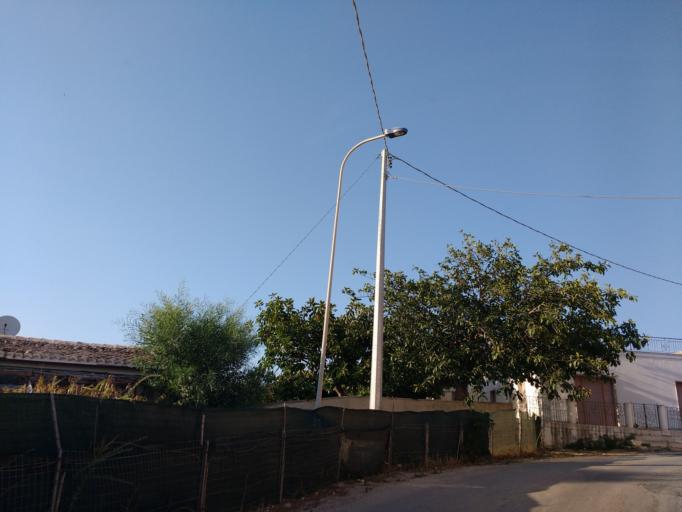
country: IT
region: Sicily
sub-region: Ragusa
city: Cava d'Aliga
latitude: 36.7298
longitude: 14.6913
